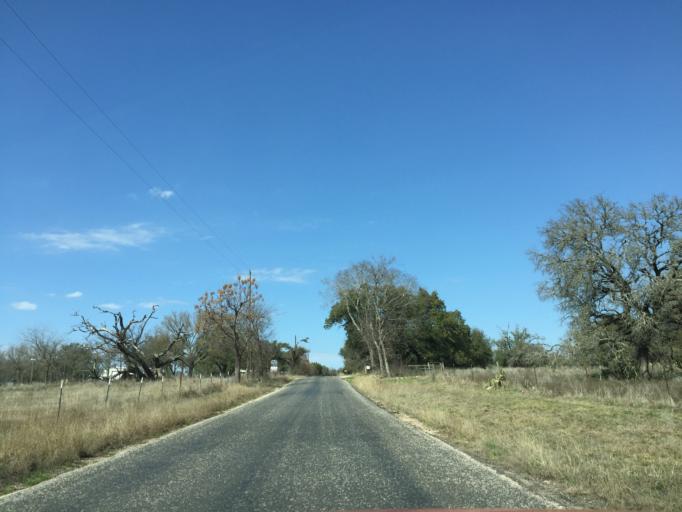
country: US
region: Texas
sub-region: Burnet County
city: Bertram
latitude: 30.7650
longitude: -97.9395
